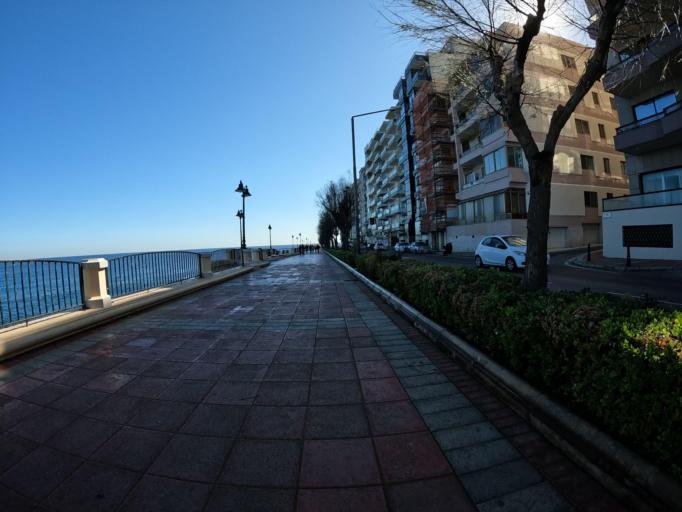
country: MT
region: Tas-Sliema
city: Sliema
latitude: 35.9169
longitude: 14.5013
